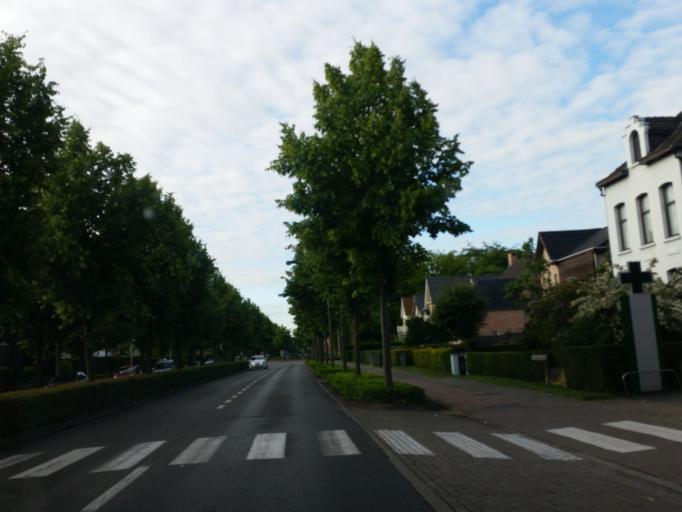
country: BE
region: Flanders
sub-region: Provincie Antwerpen
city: Brasschaat
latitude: 51.3019
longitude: 4.4865
